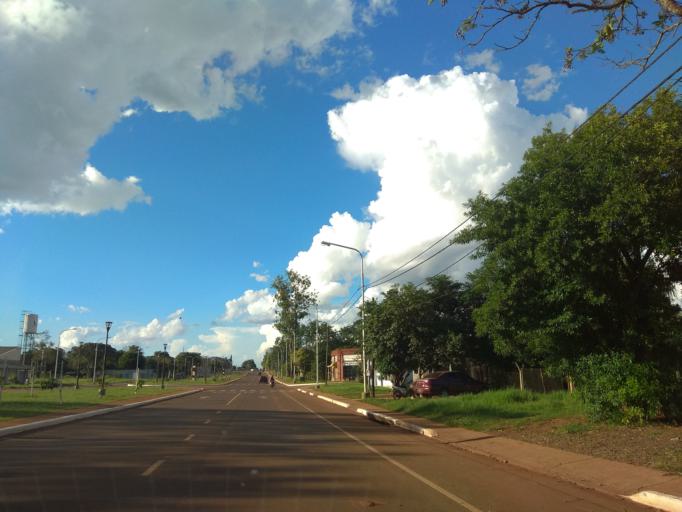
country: AR
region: Misiones
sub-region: Departamento de Candelaria
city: Candelaria
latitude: -27.4679
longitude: -55.7454
